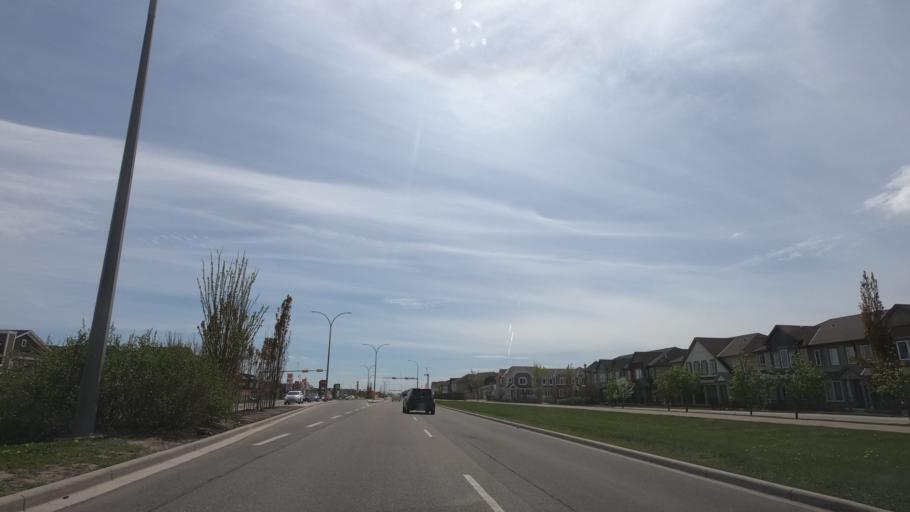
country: CA
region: Alberta
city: Airdrie
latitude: 51.2595
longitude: -114.0251
